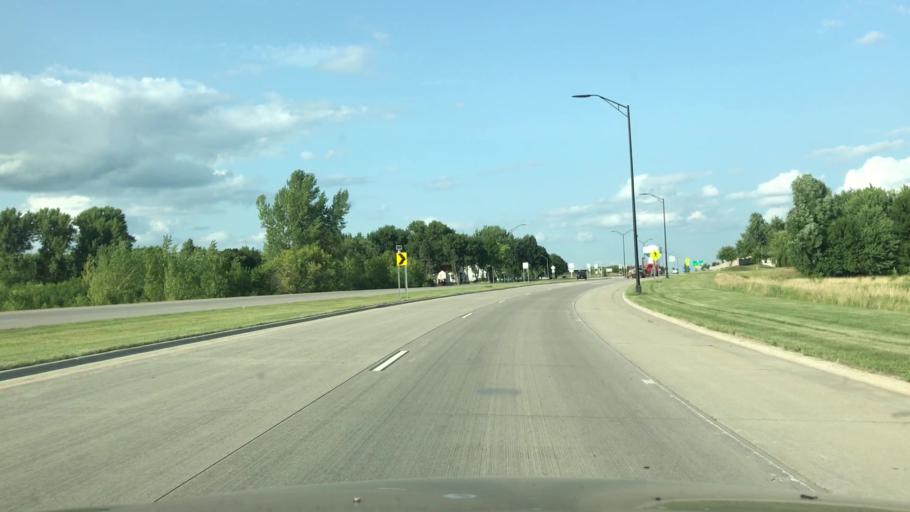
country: US
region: Minnesota
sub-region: Nobles County
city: Worthington
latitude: 43.6166
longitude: -95.5881
